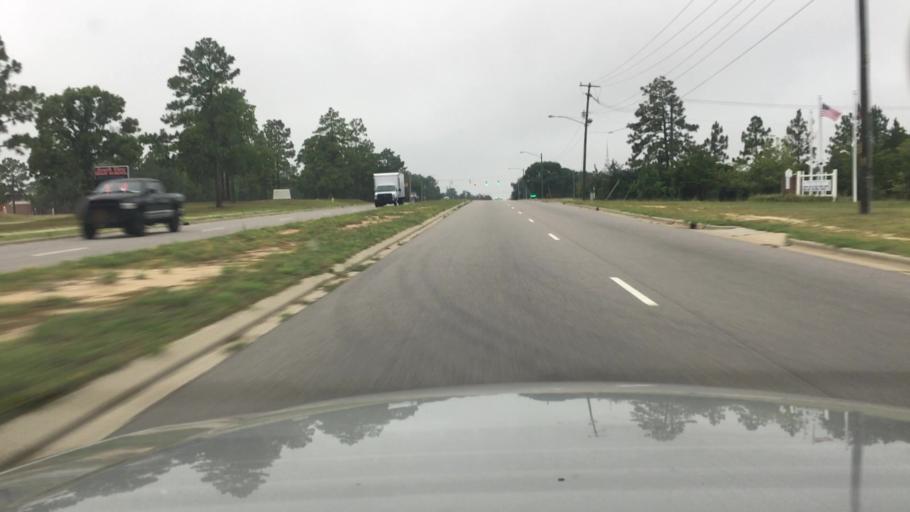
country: US
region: North Carolina
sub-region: Cumberland County
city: Hope Mills
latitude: 34.9799
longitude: -78.9260
